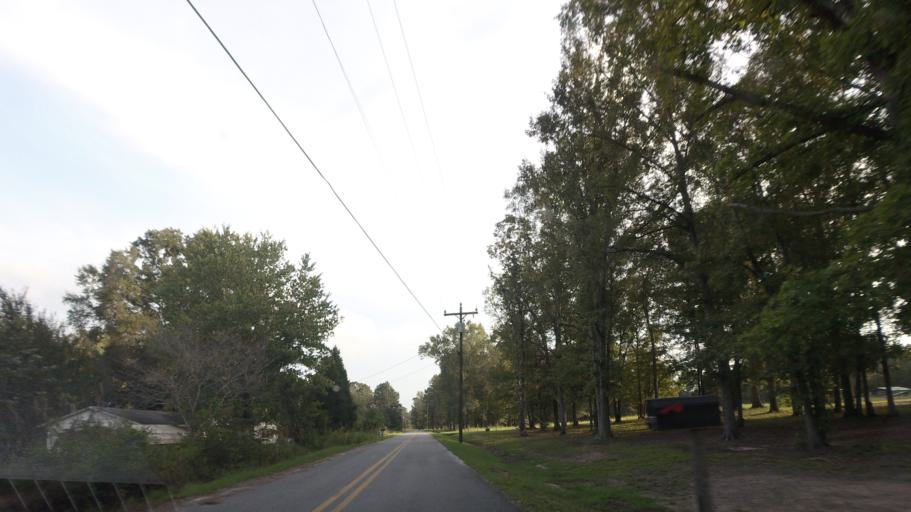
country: US
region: Georgia
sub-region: Wilkinson County
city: Gordon
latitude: 32.8291
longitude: -83.3912
